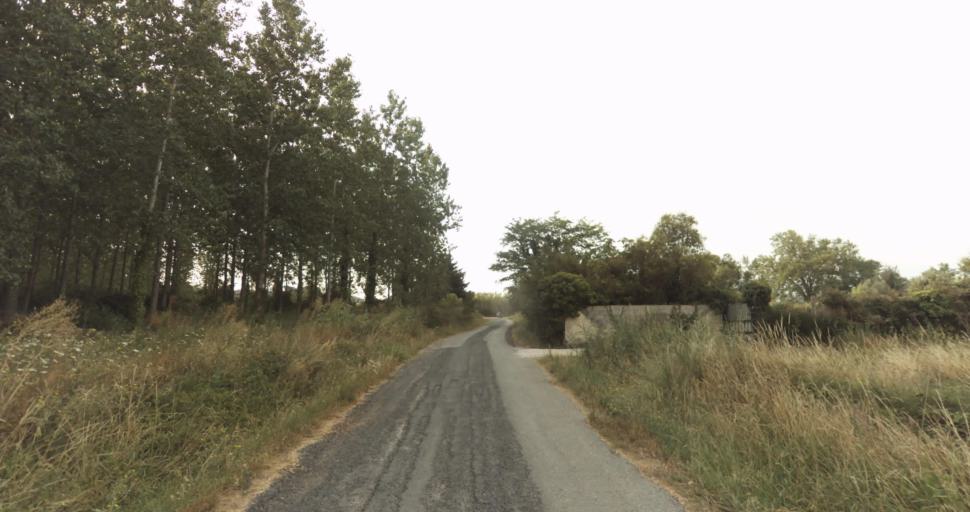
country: FR
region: Languedoc-Roussillon
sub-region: Departement des Pyrenees-Orientales
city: Corneilla-del-Vercol
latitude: 42.6275
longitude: 2.9424
